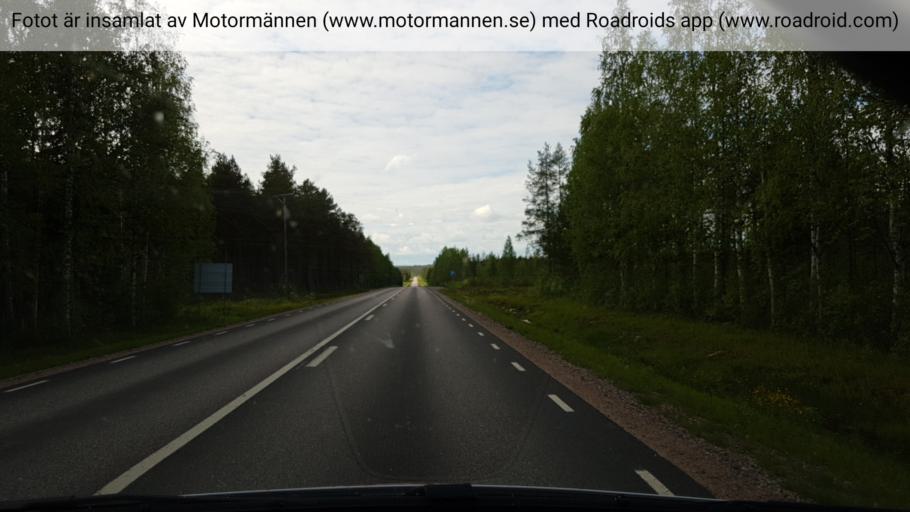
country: SE
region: Norrbotten
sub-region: Overtornea Kommun
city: OEvertornea
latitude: 66.5262
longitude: 23.7704
